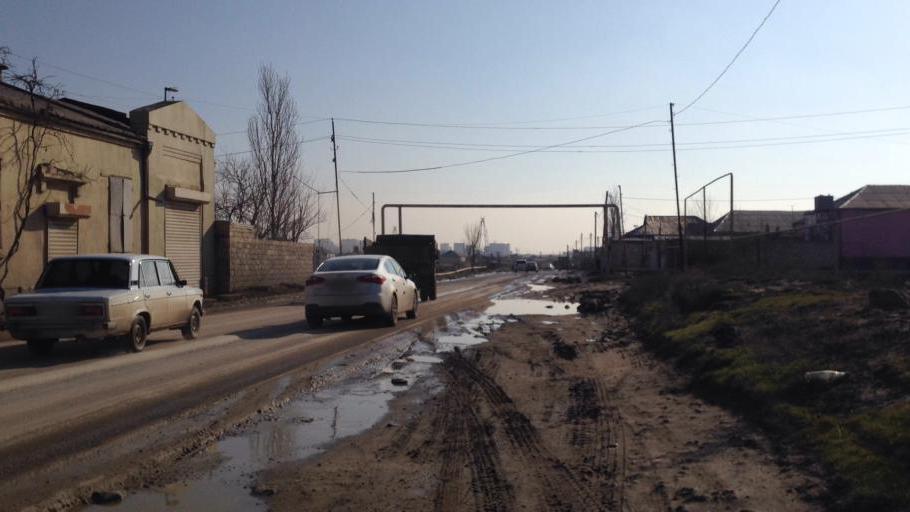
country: AZ
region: Baki
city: Balakhani
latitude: 40.4521
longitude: 49.9316
